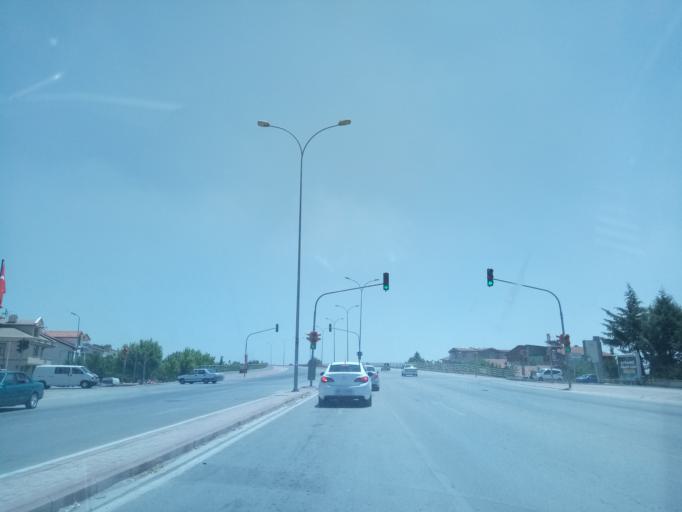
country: TR
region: Konya
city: Meram
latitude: 37.8294
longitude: 32.4900
